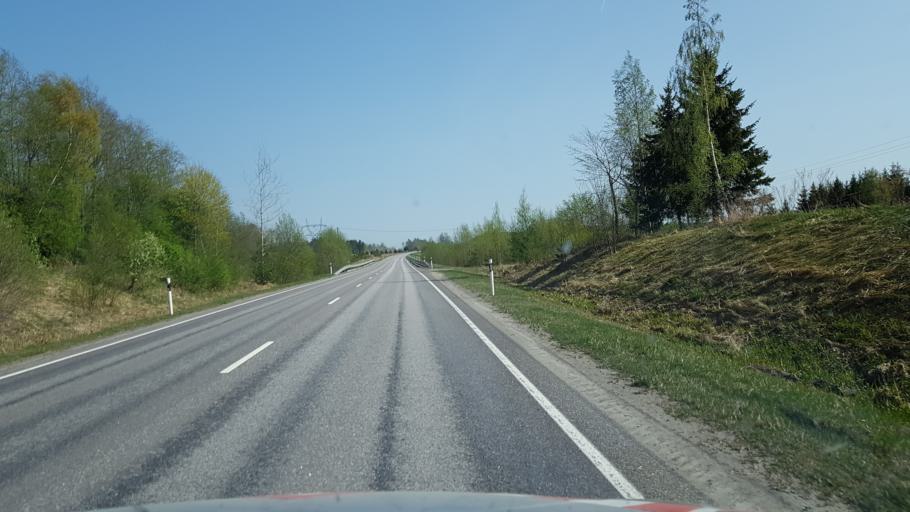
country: EE
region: Paernumaa
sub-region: Saarde vald
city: Kilingi-Nomme
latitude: 58.1622
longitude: 25.0108
